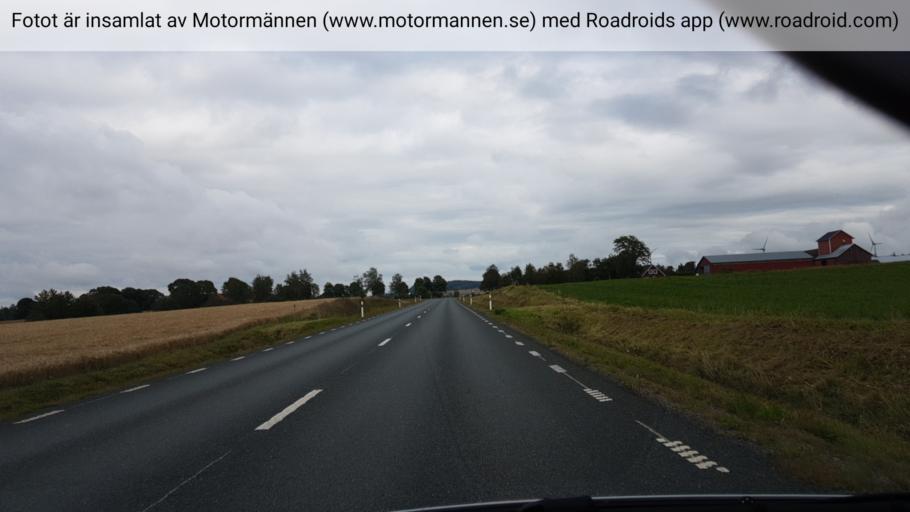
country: SE
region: Vaestra Goetaland
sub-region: Falkopings Kommun
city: Akarp
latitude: 58.1248
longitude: 13.7129
